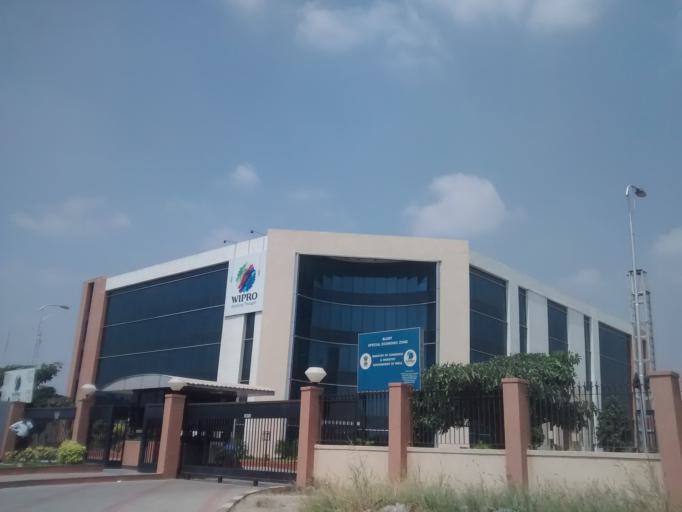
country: IN
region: Tamil Nadu
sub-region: Coimbatore
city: Singanallur
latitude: 11.0306
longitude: 77.0177
